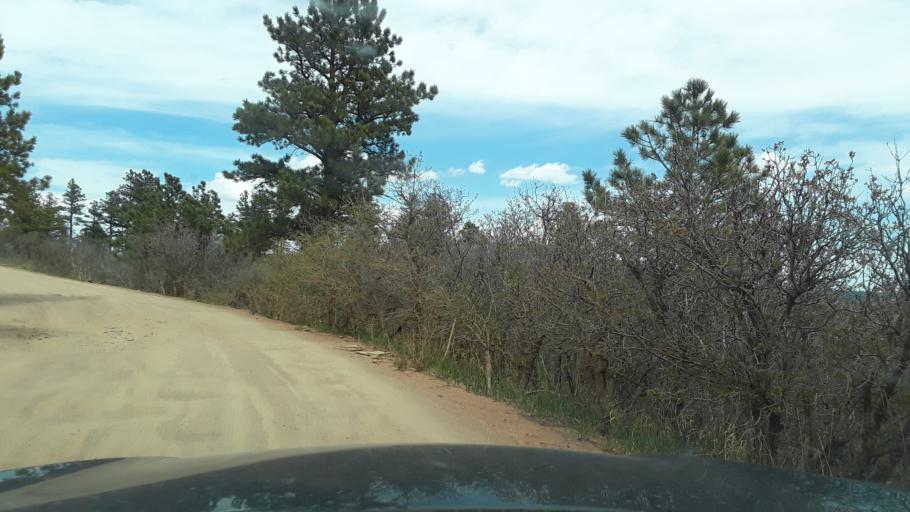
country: US
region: Colorado
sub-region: El Paso County
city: Palmer Lake
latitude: 39.0862
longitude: -104.9115
